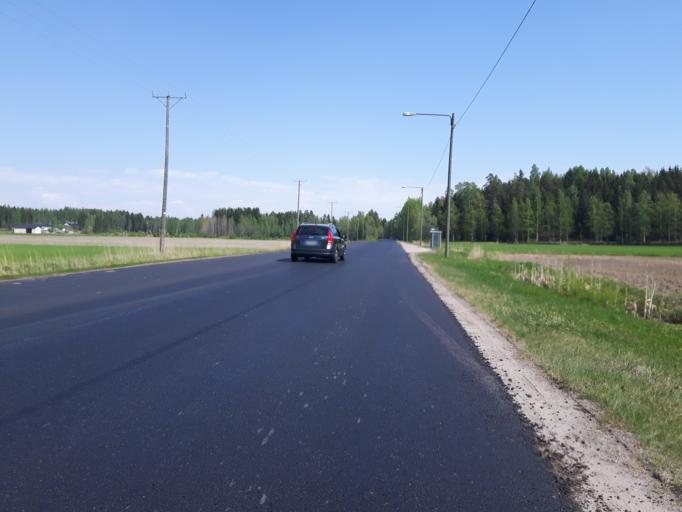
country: FI
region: Uusimaa
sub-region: Helsinki
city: Pornainen
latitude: 60.3331
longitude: 25.4530
